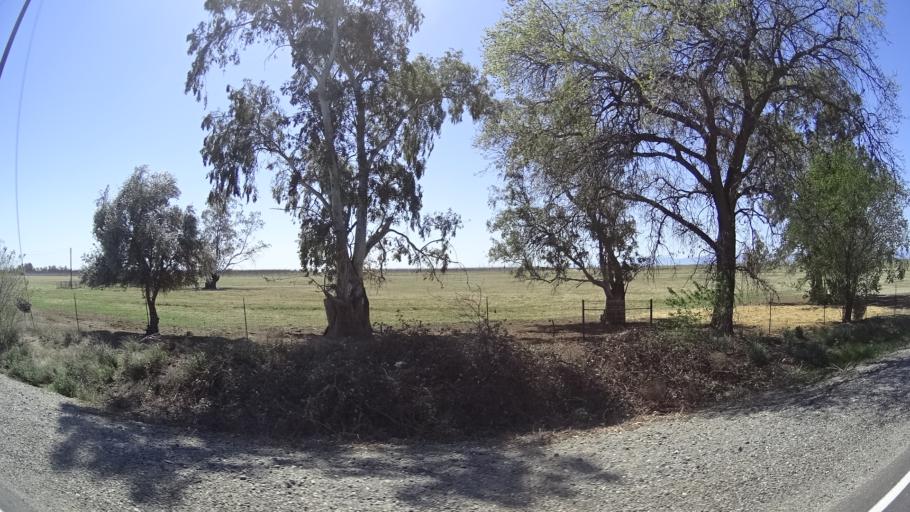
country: US
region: California
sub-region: Glenn County
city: Orland
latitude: 39.7698
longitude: -122.2573
